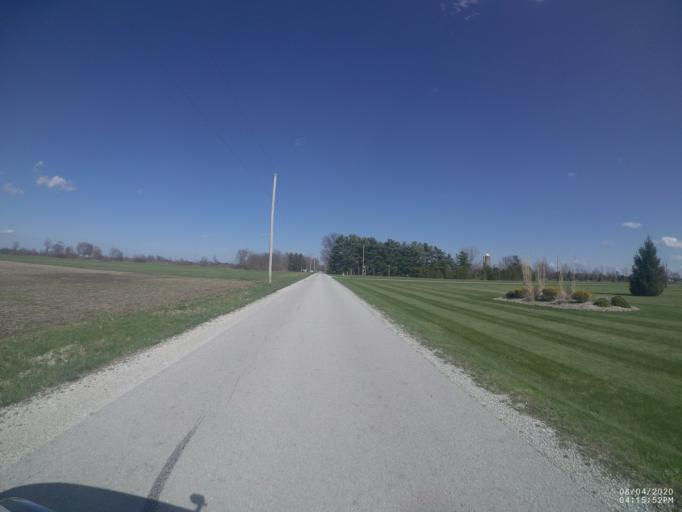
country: US
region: Ohio
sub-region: Sandusky County
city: Stony Prairie
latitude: 41.2981
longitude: -83.1951
